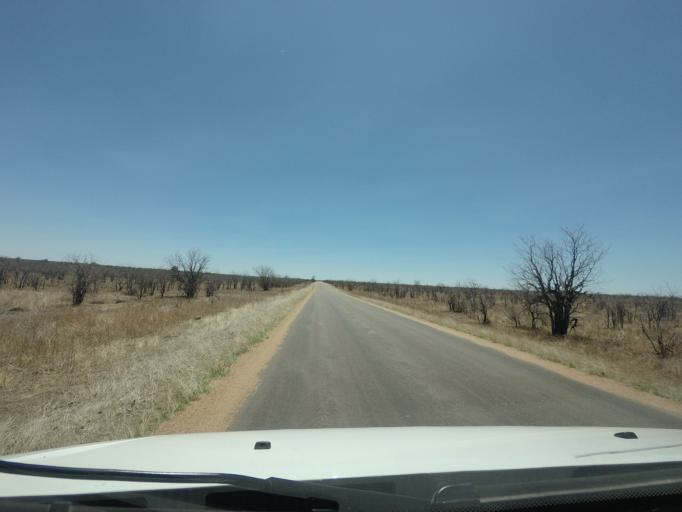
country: ZA
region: Limpopo
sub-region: Mopani District Municipality
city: Phalaborwa
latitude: -23.5781
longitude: 31.4508
